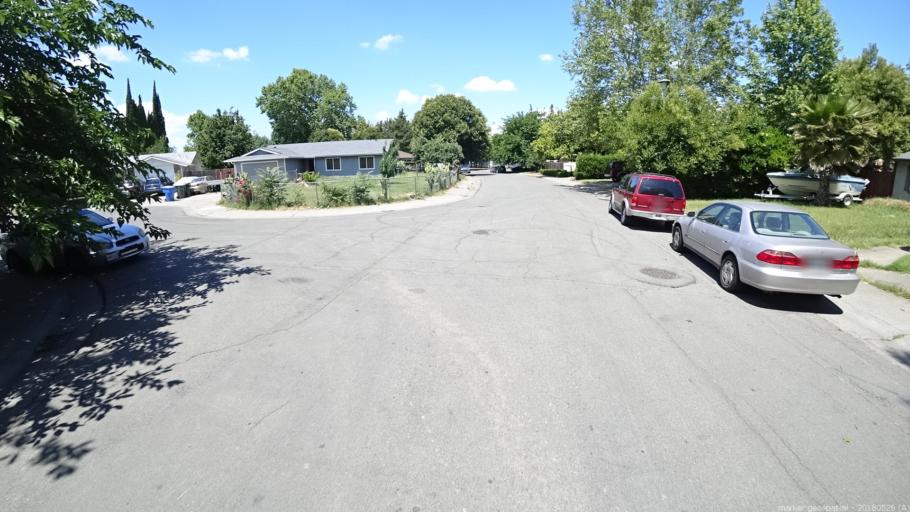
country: US
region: California
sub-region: Sacramento County
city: Sacramento
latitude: 38.6150
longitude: -121.4904
